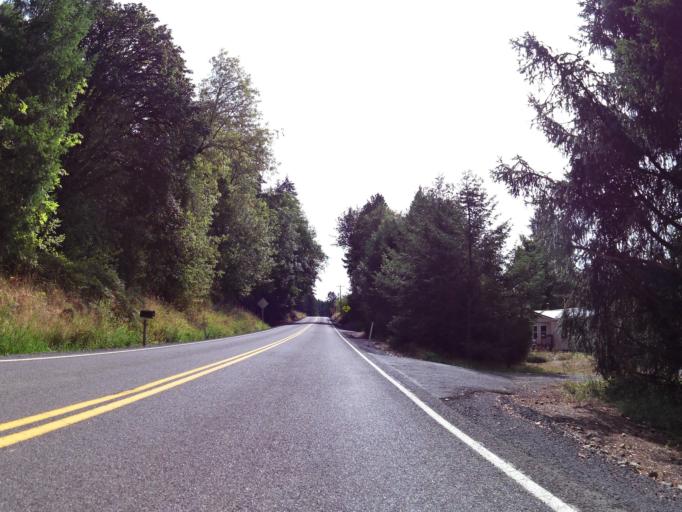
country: US
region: Washington
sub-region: Lewis County
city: Napavine
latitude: 46.5753
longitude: -122.9719
